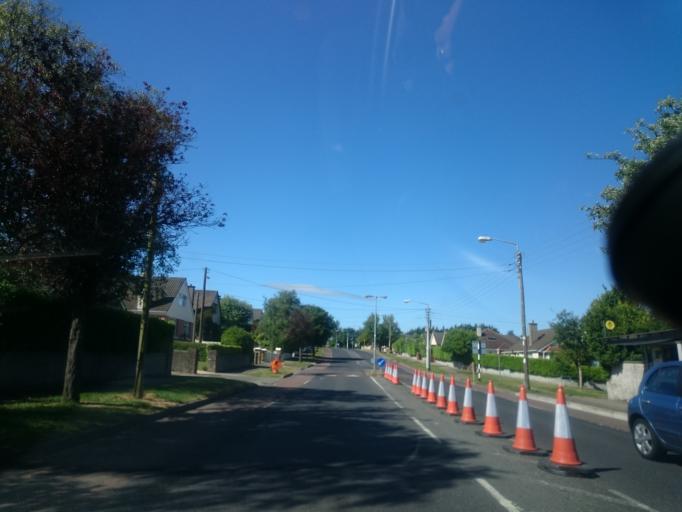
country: IE
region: Leinster
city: Sallynoggin
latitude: 53.2720
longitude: -6.1272
